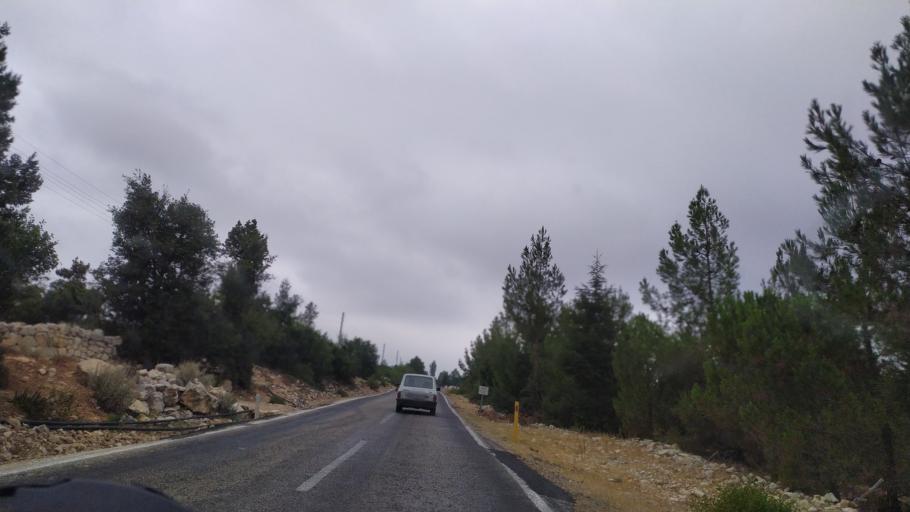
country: TR
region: Mersin
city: Silifke
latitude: 36.5476
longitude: 33.9230
